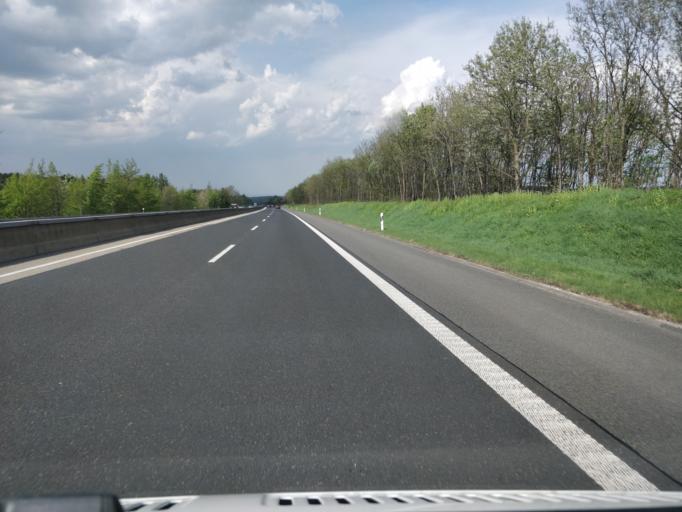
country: DE
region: North Rhine-Westphalia
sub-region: Regierungsbezirk Koln
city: Mechernich
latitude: 50.5448
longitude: 6.6781
